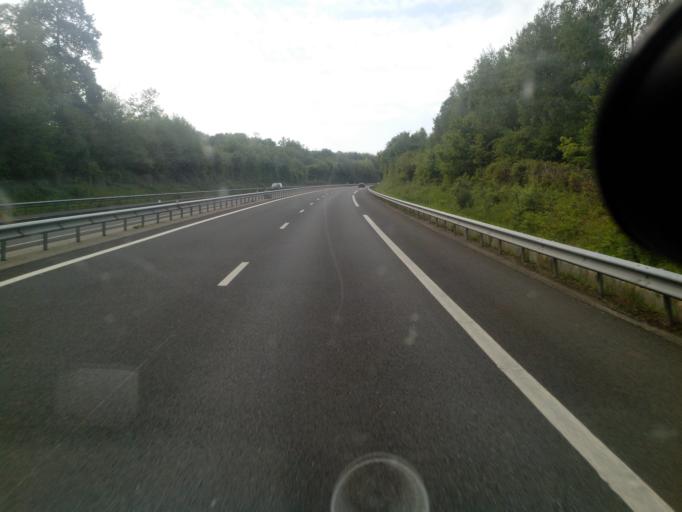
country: FR
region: Lower Normandy
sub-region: Departement du Calvados
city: Saint-Gatien-des-Bois
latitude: 49.3484
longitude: 0.2197
